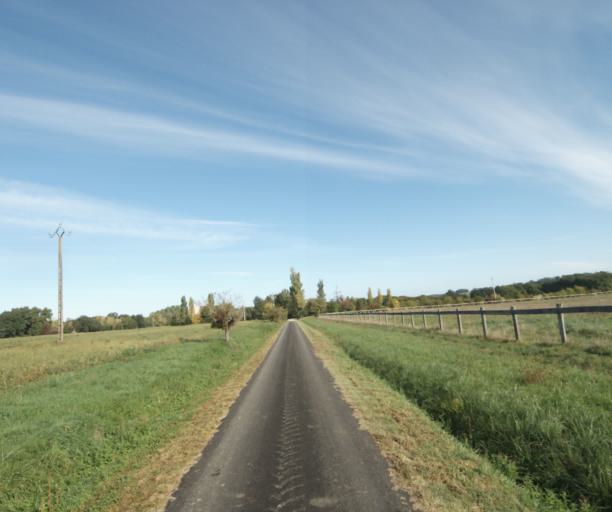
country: FR
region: Midi-Pyrenees
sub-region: Departement du Gers
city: Montreal
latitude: 43.9427
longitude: 0.1263
